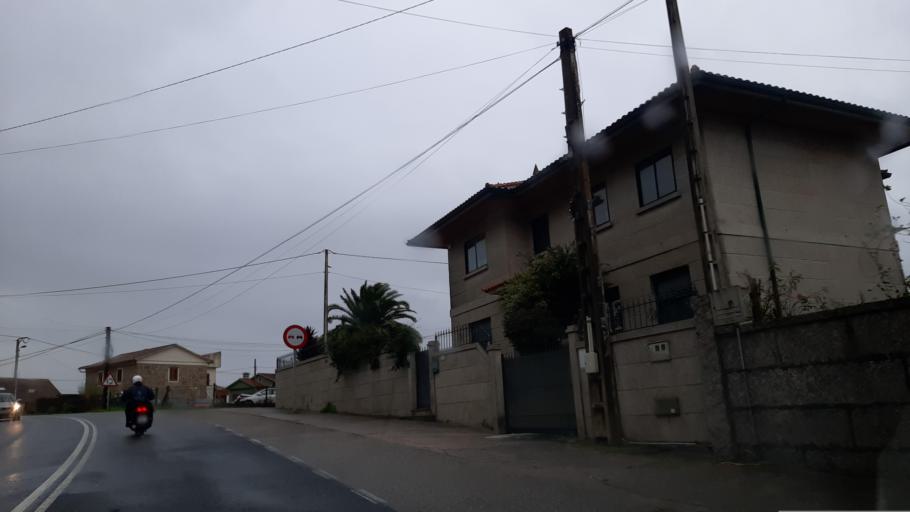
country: ES
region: Galicia
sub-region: Provincia de Pontevedra
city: Nigran
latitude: 42.1699
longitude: -8.8007
